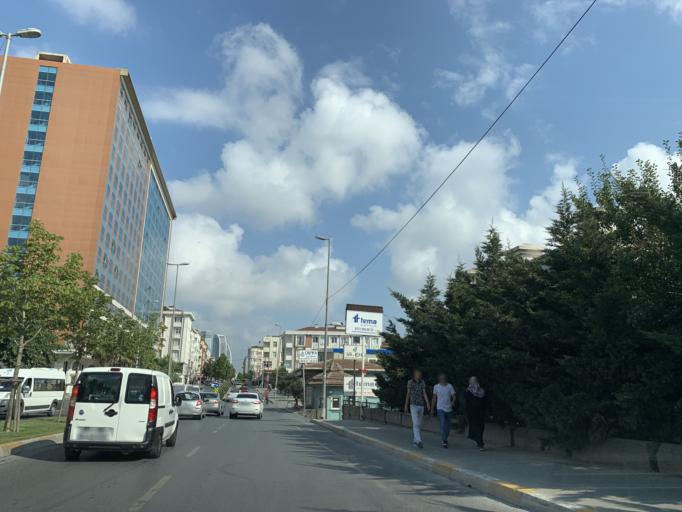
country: TR
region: Istanbul
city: Esenyurt
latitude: 41.0263
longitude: 28.6682
